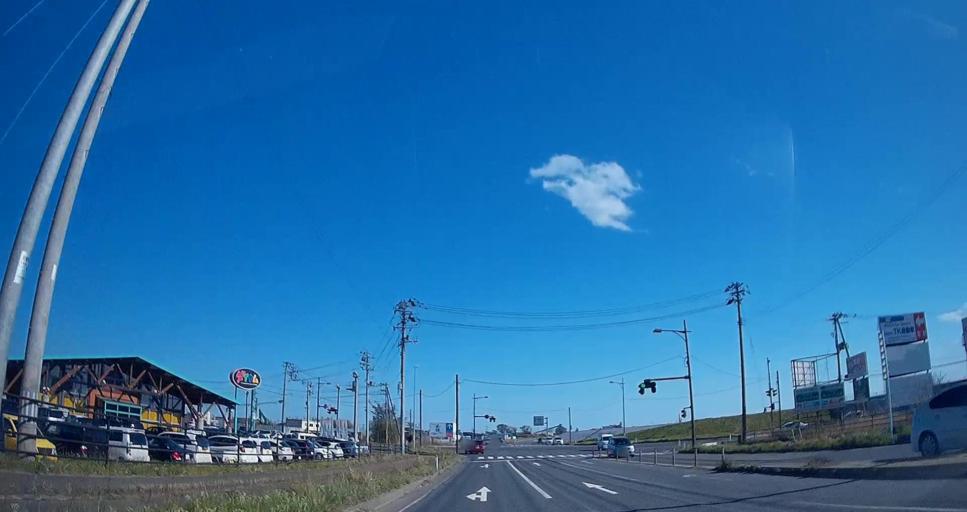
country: JP
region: Miyagi
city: Yamoto
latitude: 38.4320
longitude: 141.2484
